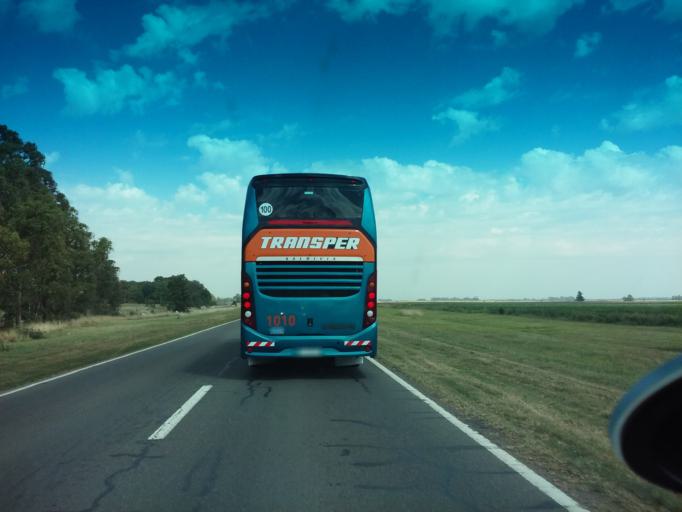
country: AR
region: Buenos Aires
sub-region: Partido de Carlos Casares
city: Carlos Casares
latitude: -35.6502
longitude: -61.3835
